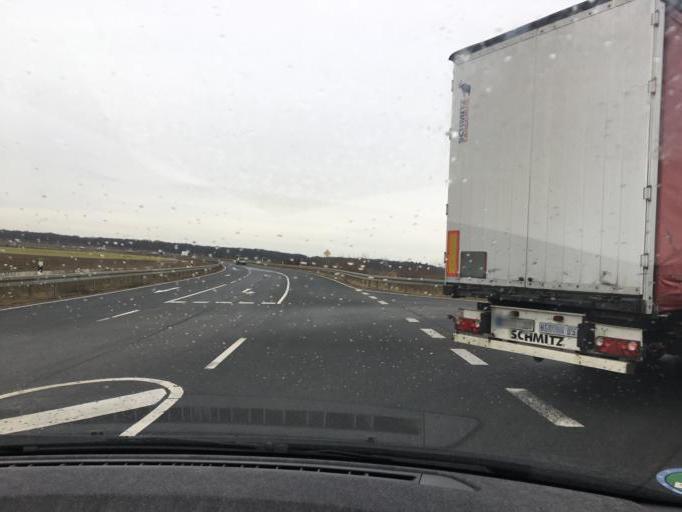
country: DE
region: North Rhine-Westphalia
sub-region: Regierungsbezirk Koln
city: Bergheim
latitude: 50.9079
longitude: 6.6160
